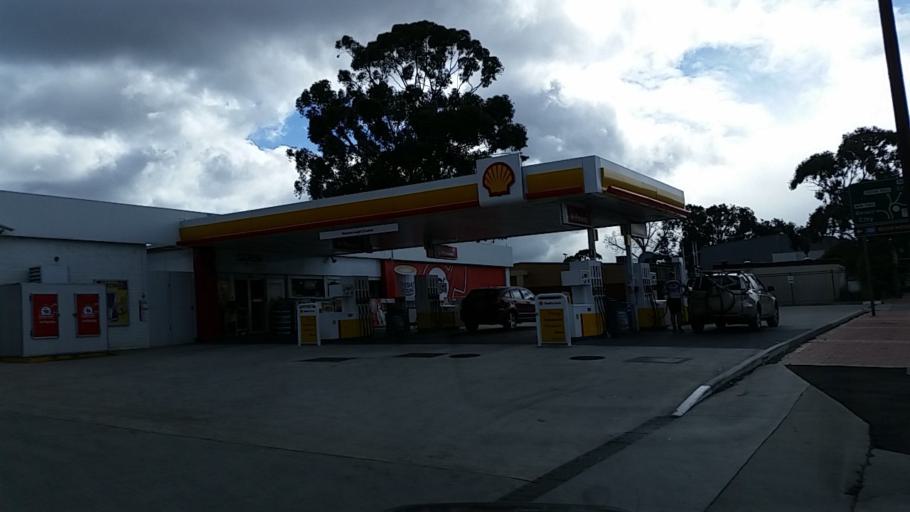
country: AU
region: South Australia
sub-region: Mitcham
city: Blackwood
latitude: -35.0212
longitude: 138.6153
